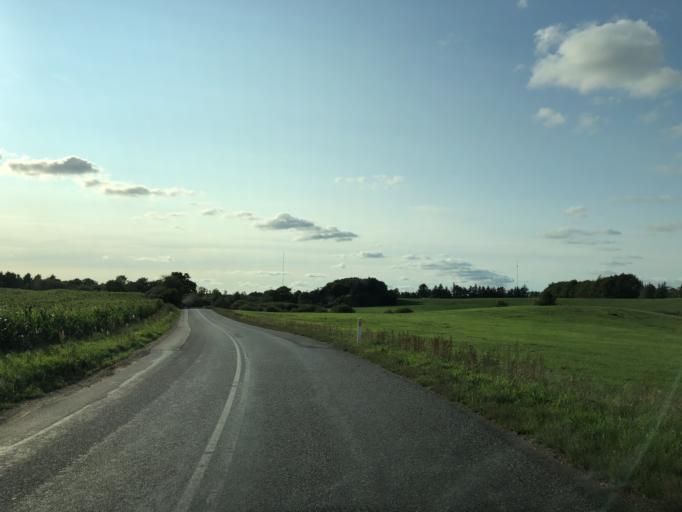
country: DK
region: Central Jutland
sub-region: Viborg Kommune
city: Viborg
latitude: 56.4505
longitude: 9.2923
